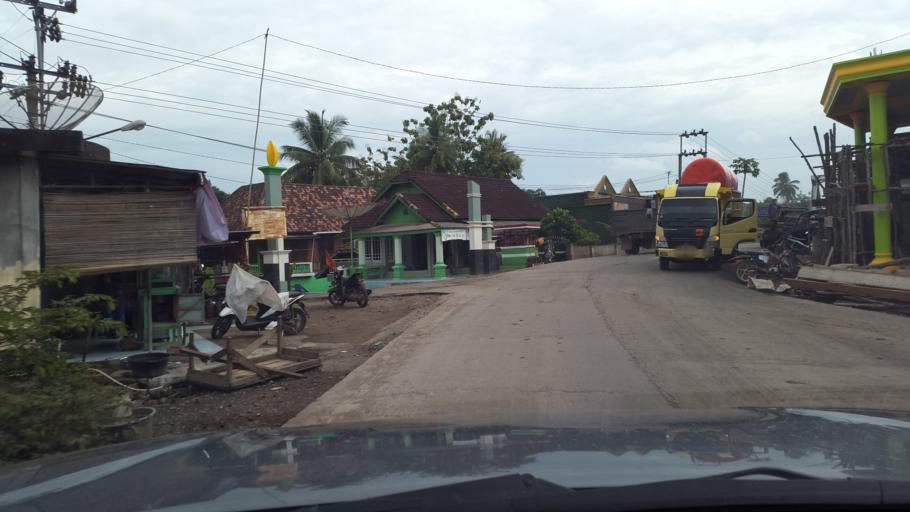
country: ID
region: South Sumatra
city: Gunungmegang Dalam
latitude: -3.4156
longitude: 103.9724
